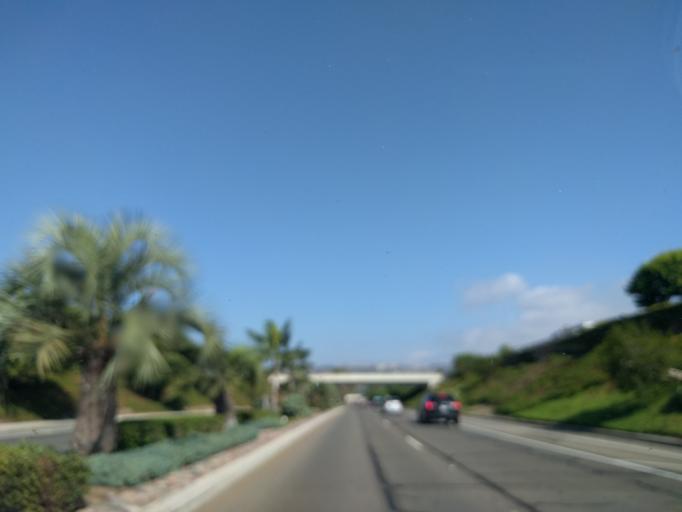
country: US
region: California
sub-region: Orange County
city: Dana Point
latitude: 33.4728
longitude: -117.7145
